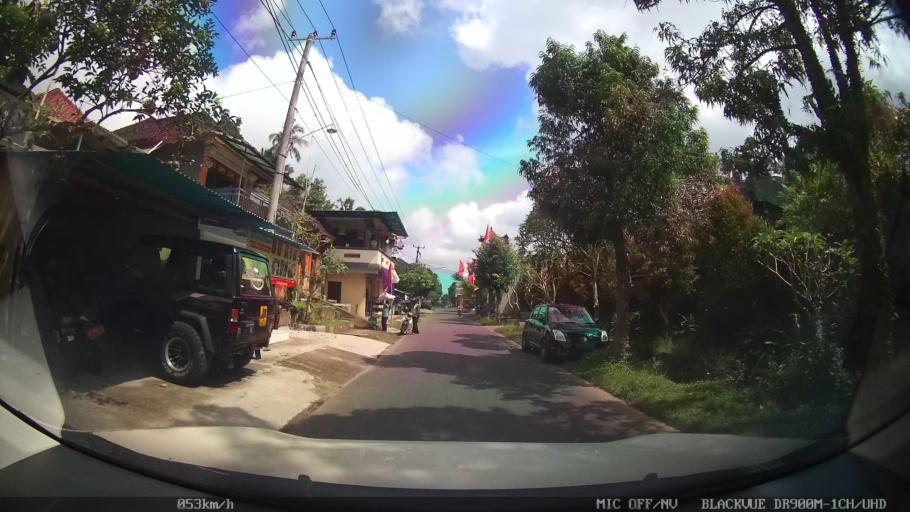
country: ID
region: Bali
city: Banjar Madangan Kaja
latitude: -8.4743
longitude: 115.3242
